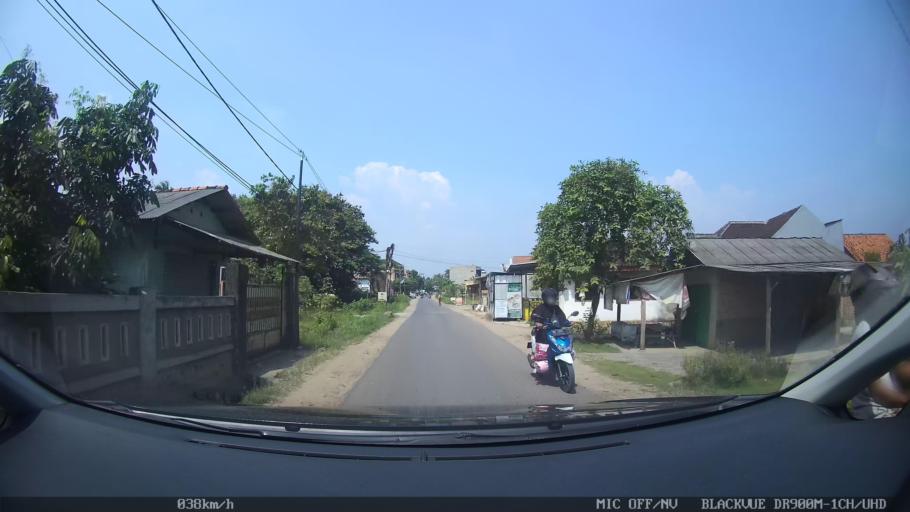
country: ID
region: Lampung
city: Natar
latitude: -5.3102
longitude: 105.2015
